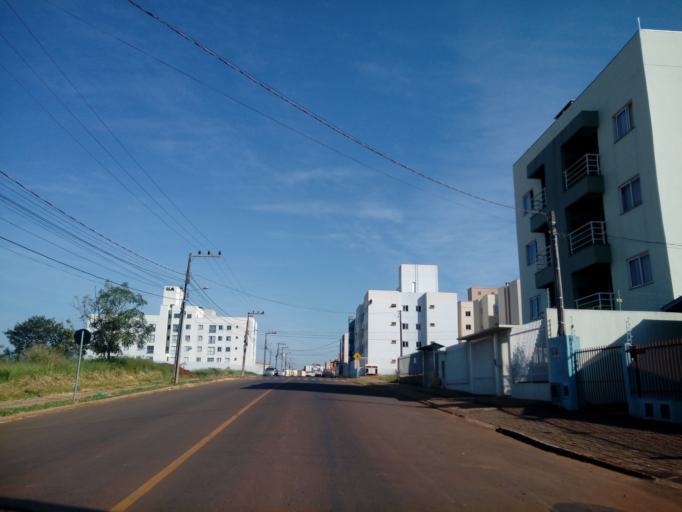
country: BR
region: Santa Catarina
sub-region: Chapeco
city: Chapeco
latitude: -27.0951
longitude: -52.6685
